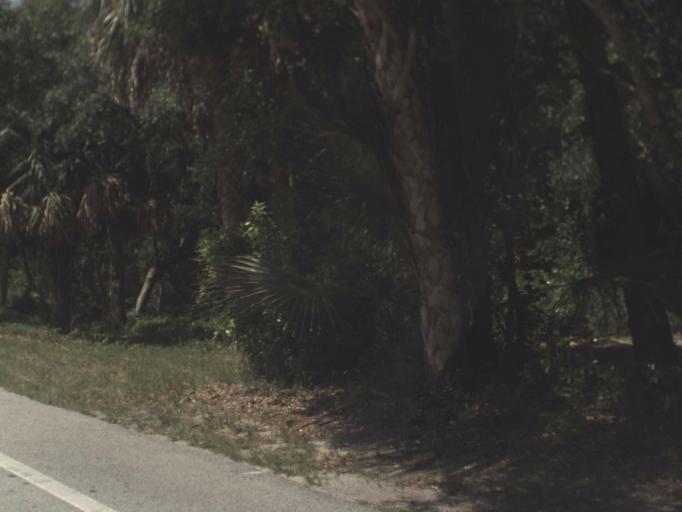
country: US
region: Florida
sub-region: Saint Johns County
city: Palm Valley
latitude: 30.1358
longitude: -81.3506
